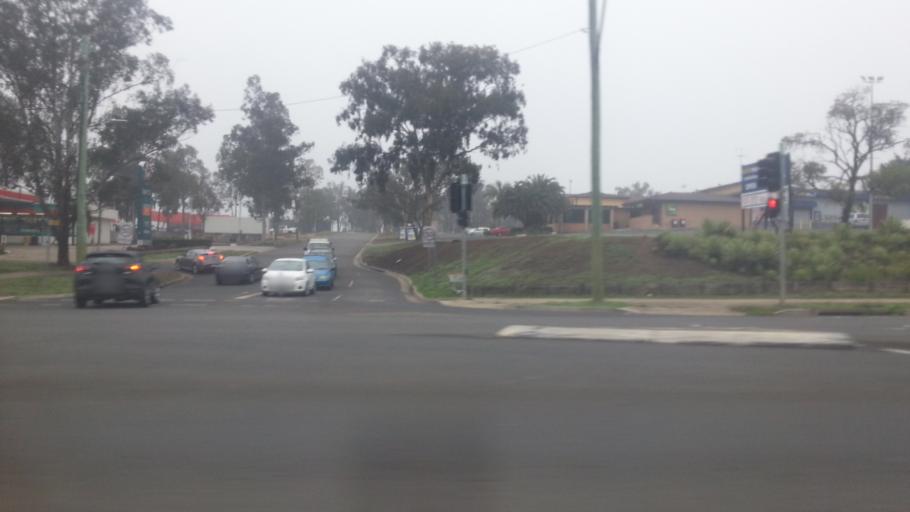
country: AU
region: New South Wales
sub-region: Penrith Municipality
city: Cambridge Park
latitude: -33.7411
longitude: 150.7162
